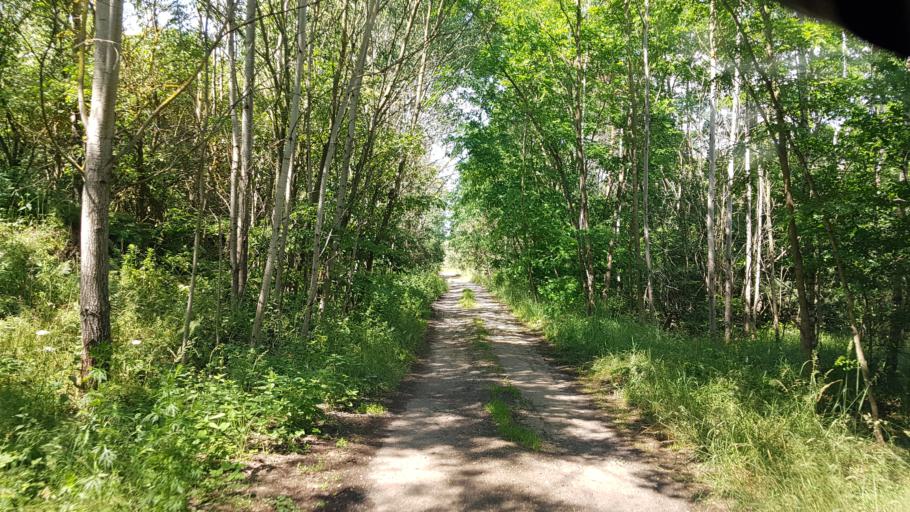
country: DE
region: Brandenburg
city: Sallgast
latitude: 51.5930
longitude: 13.7900
